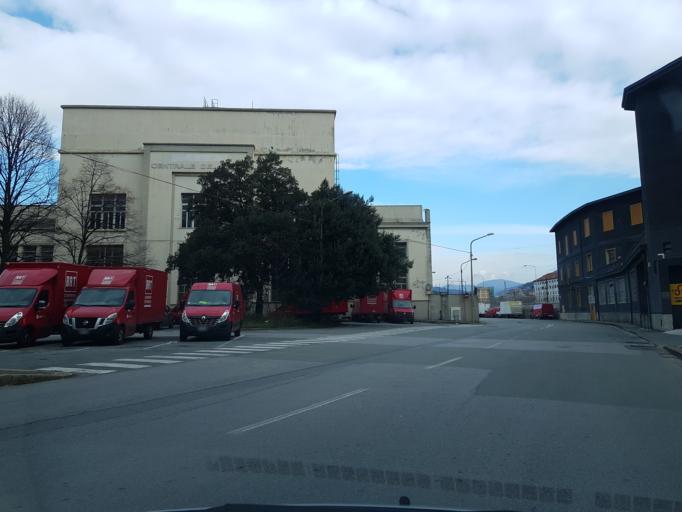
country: IT
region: Liguria
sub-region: Provincia di Genova
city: Genoa
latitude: 44.4438
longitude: 8.8885
